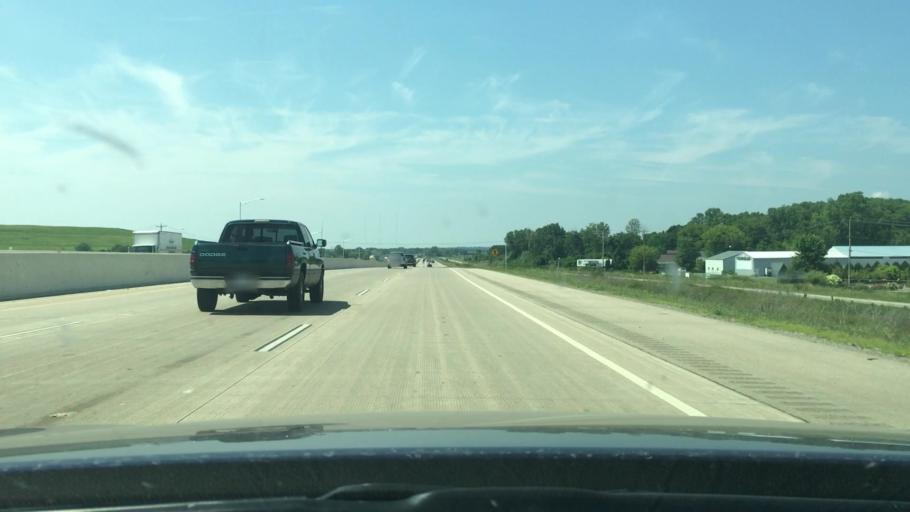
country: US
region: Wisconsin
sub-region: Winnebago County
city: Oshkosh
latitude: 44.0964
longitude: -88.5442
